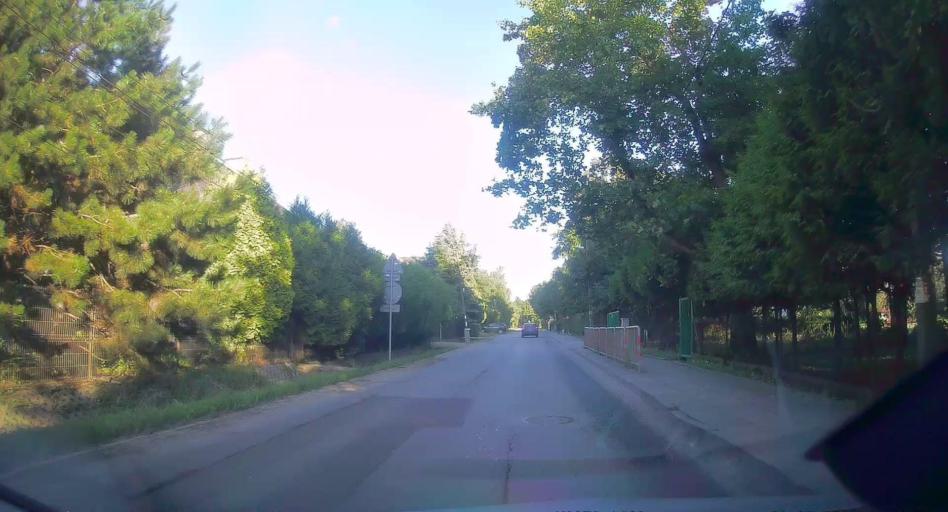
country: PL
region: Lesser Poland Voivodeship
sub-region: Powiat wielicki
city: Czarnochowice
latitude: 50.0188
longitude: 20.0416
